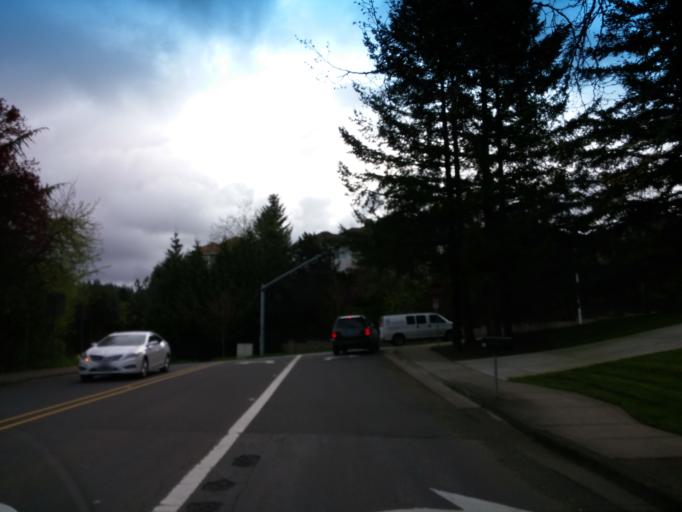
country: US
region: Oregon
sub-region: Washington County
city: Cedar Mill
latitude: 45.5368
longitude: -122.8127
